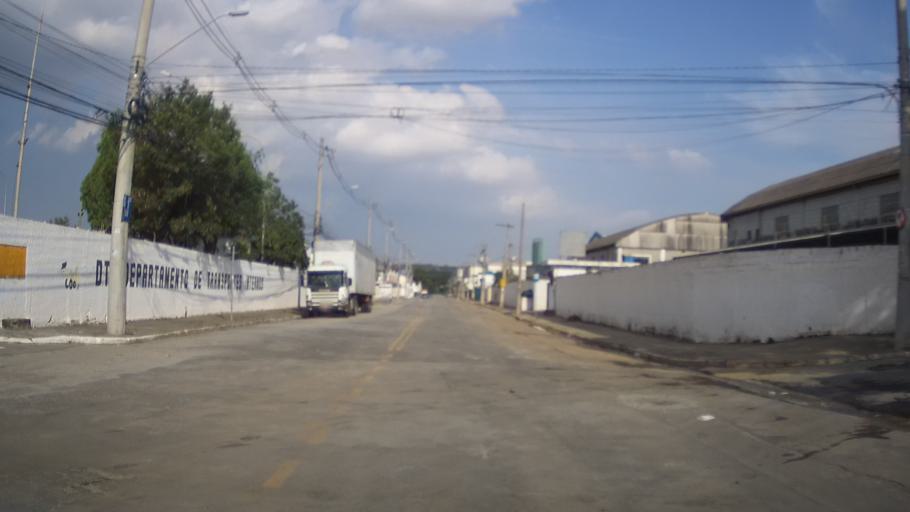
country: BR
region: Sao Paulo
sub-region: Guarulhos
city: Guarulhos
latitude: -23.4405
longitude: -46.5020
